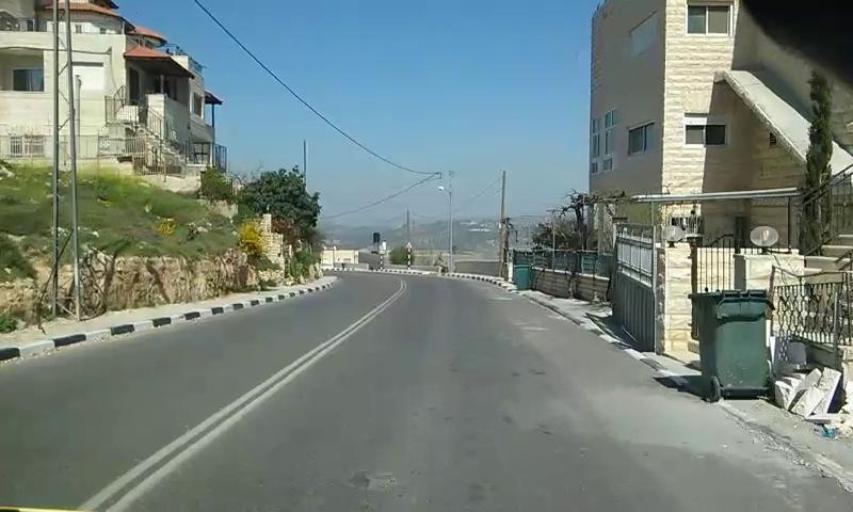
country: PS
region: West Bank
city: Husan
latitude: 31.7077
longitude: 35.1483
